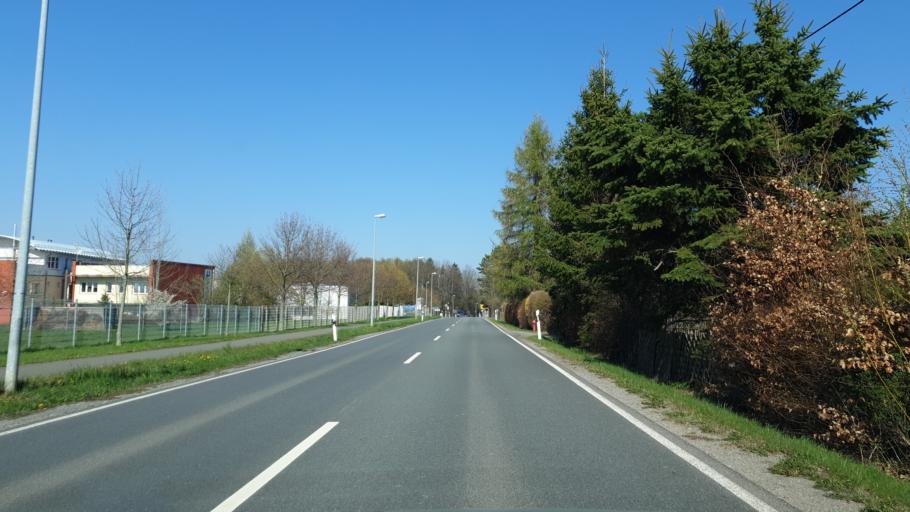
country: DE
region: Saxony
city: Oelsnitz
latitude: 50.7160
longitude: 12.7177
